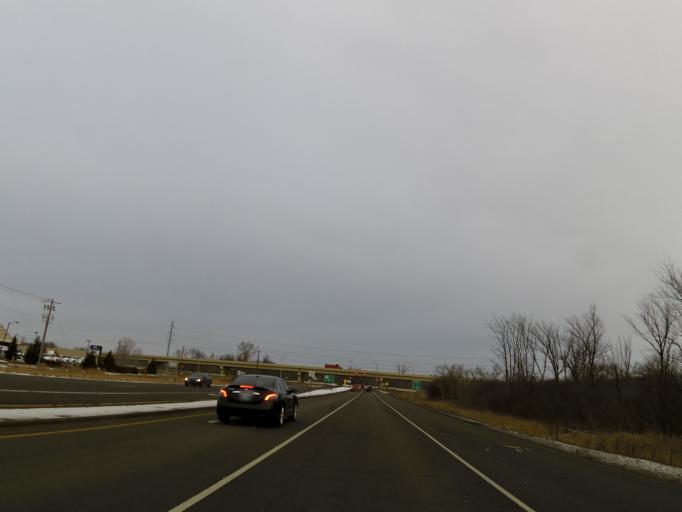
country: US
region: Minnesota
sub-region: Scott County
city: Savage
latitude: 44.7768
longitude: -93.3782
